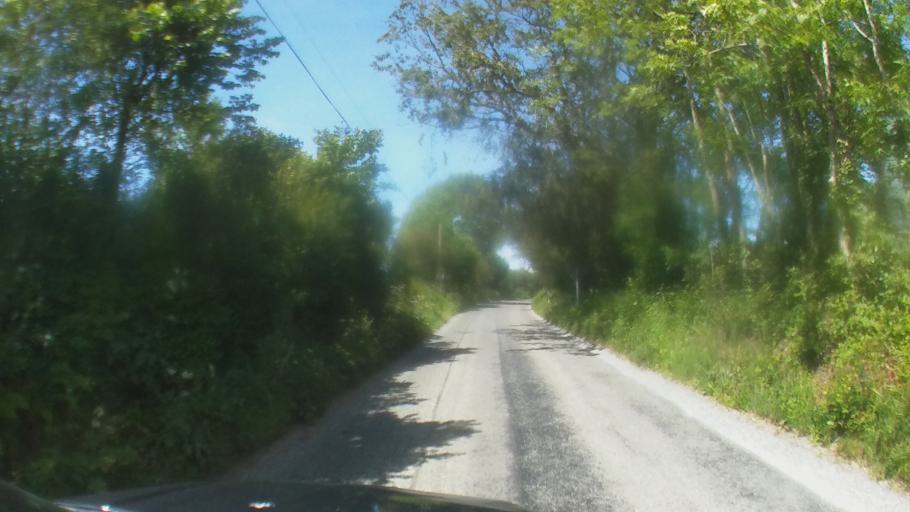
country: IE
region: Leinster
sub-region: Loch Garman
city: Loch Garman
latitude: 52.2314
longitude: -6.5555
